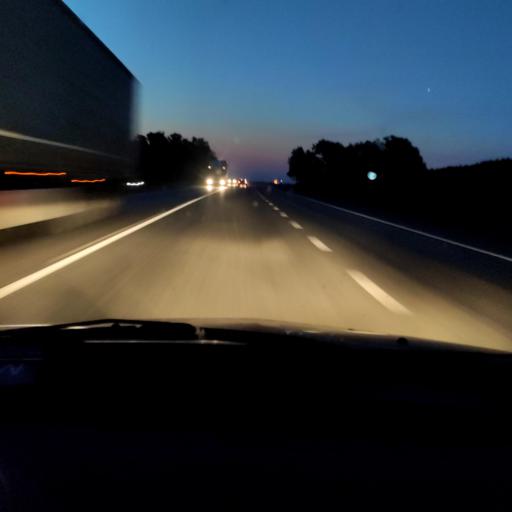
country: RU
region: Bashkortostan
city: Iglino
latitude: 54.7279
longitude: 56.2508
